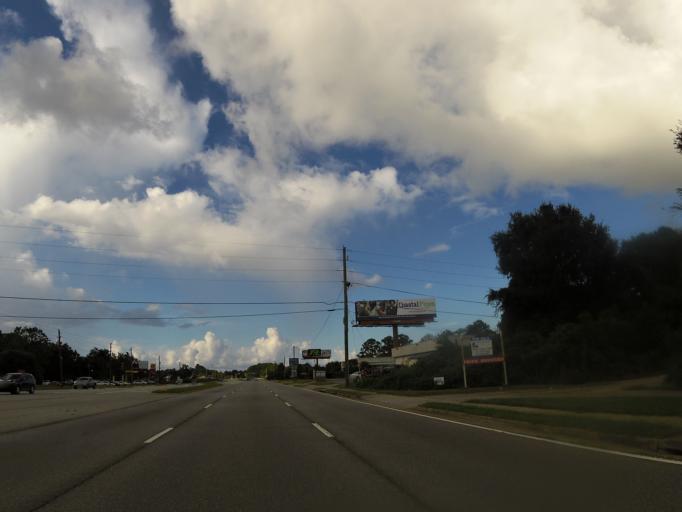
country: US
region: Georgia
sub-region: Glynn County
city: Brunswick
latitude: 31.1774
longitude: -81.4730
